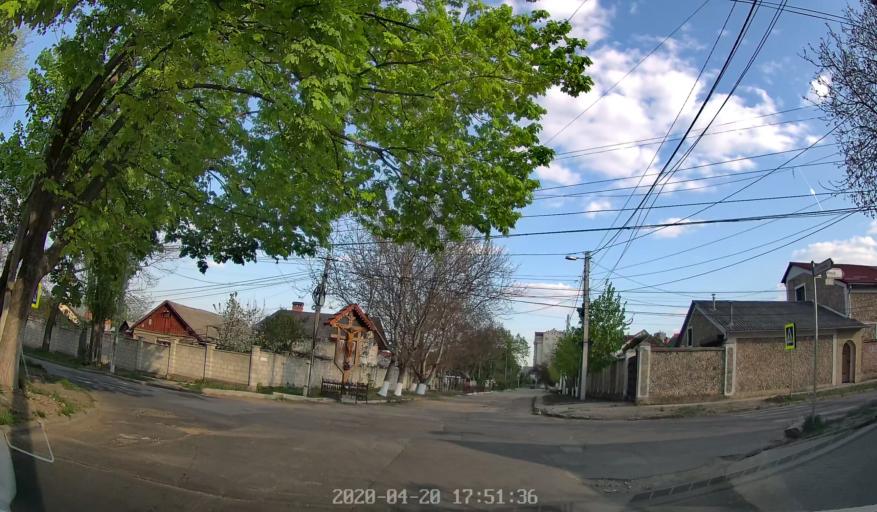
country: MD
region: Chisinau
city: Chisinau
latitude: 46.9999
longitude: 28.8654
